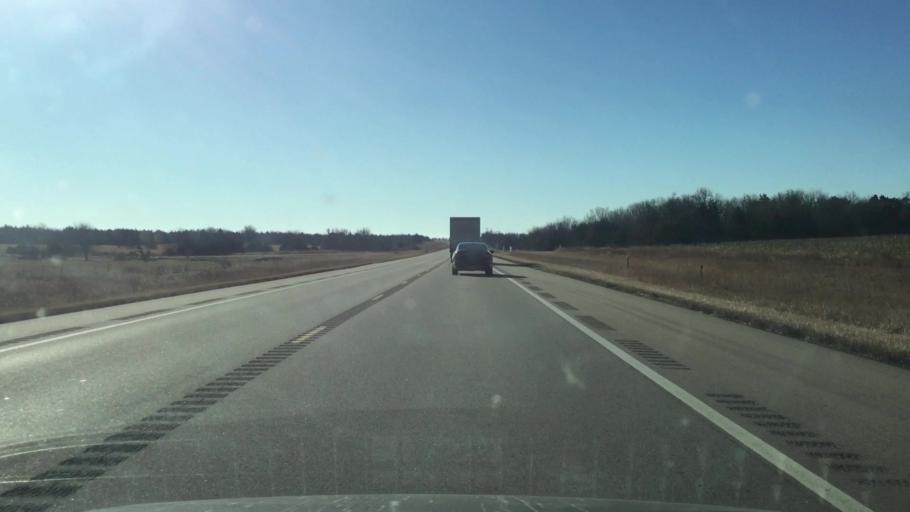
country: US
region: Kansas
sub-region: Allen County
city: Iola
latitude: 38.0406
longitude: -95.3806
